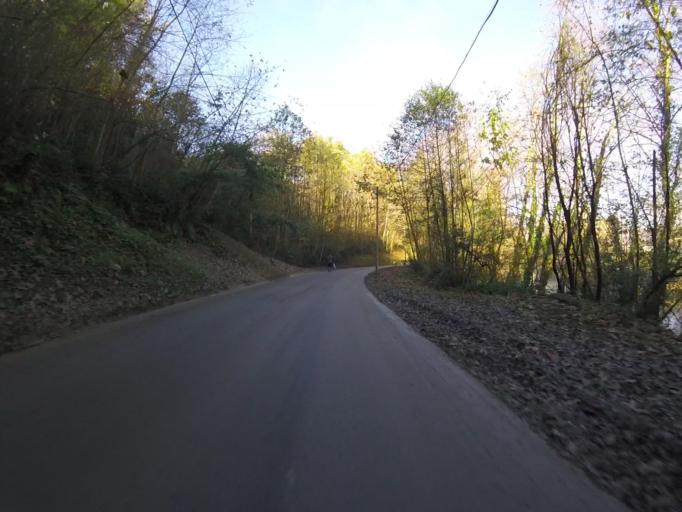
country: ES
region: Basque Country
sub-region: Provincia de Guipuzcoa
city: Usurbil
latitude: 43.2630
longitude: -2.0529
